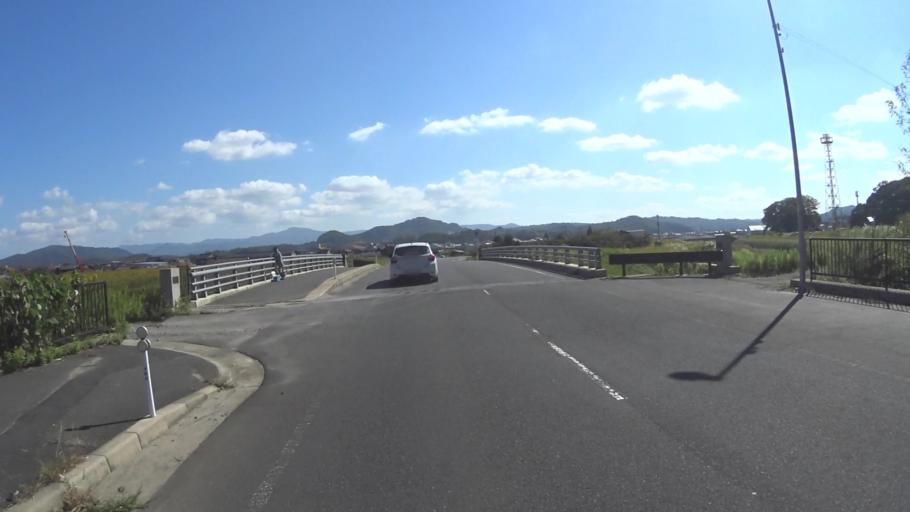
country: JP
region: Kyoto
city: Miyazu
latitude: 35.6846
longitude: 135.0163
